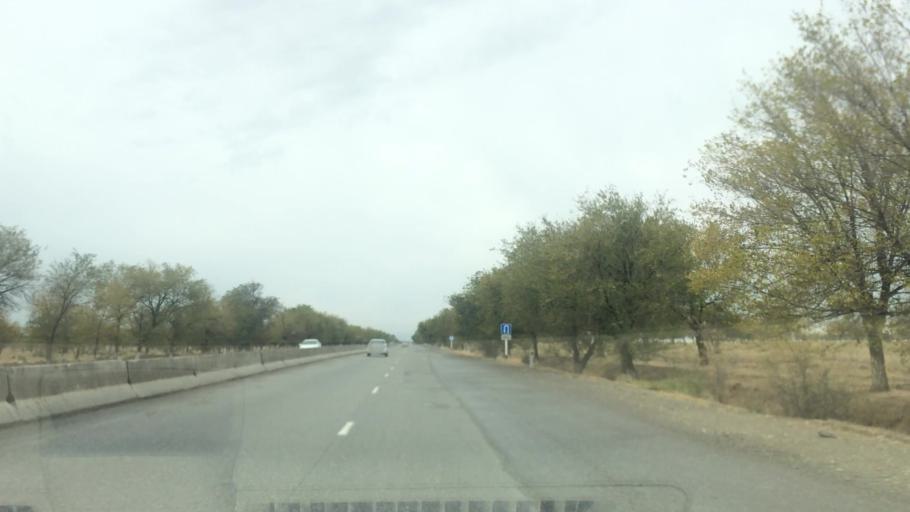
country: UZ
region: Samarqand
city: Bulung'ur
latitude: 39.8095
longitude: 67.3636
